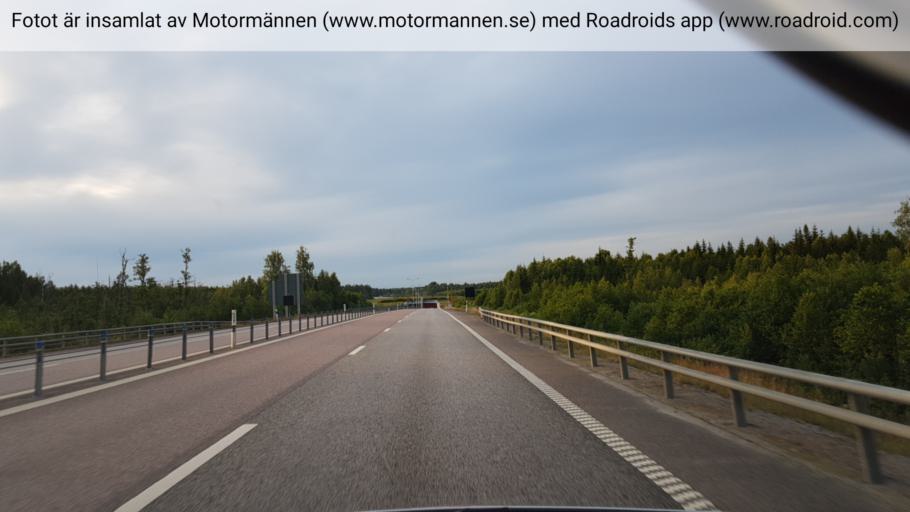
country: SE
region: Vaestra Goetaland
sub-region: Skovde Kommun
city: Skultorp
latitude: 58.3483
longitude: 13.8654
